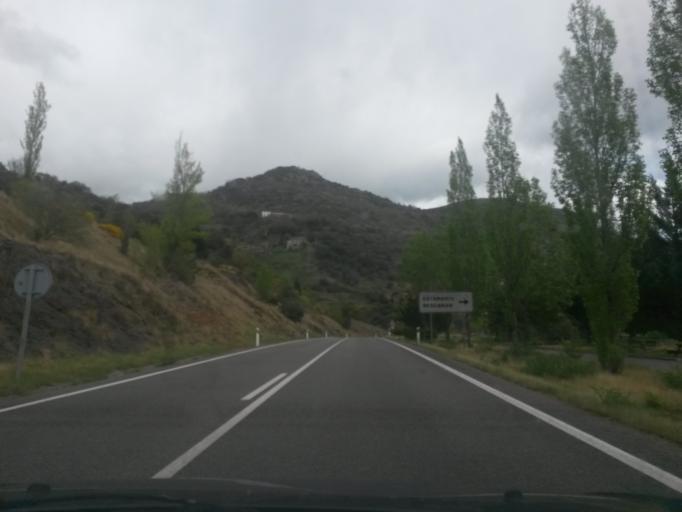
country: ES
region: Catalonia
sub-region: Provincia de Lleida
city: Alas i Cerc
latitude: 42.3594
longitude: 1.5115
